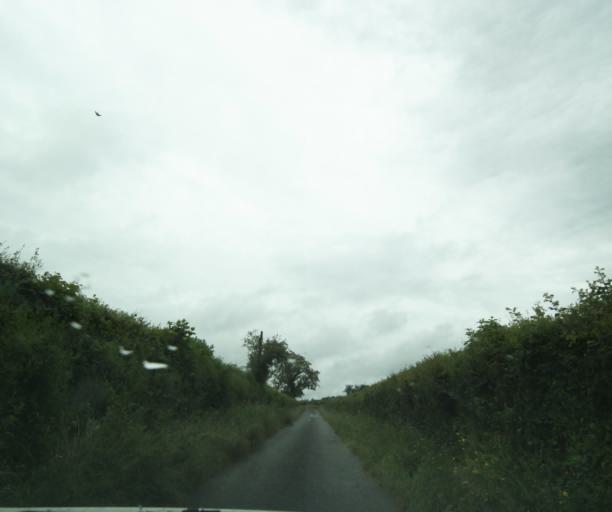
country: FR
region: Bourgogne
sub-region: Departement de Saone-et-Loire
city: Palinges
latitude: 46.5290
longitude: 4.2597
